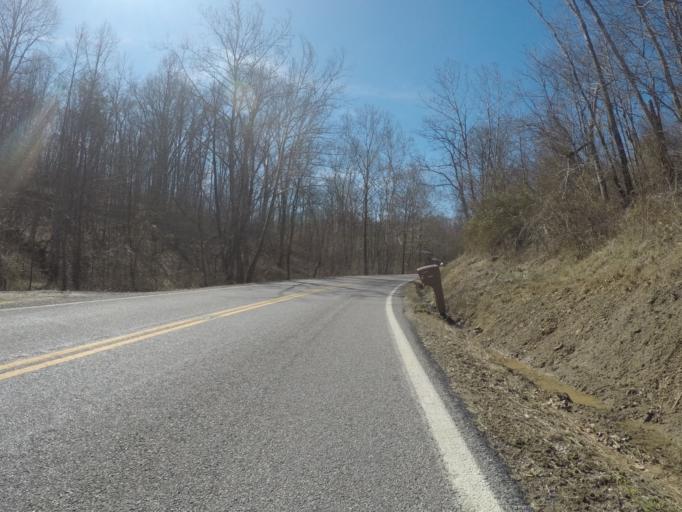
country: US
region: Ohio
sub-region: Lawrence County
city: Burlington
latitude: 38.4908
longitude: -82.5423
